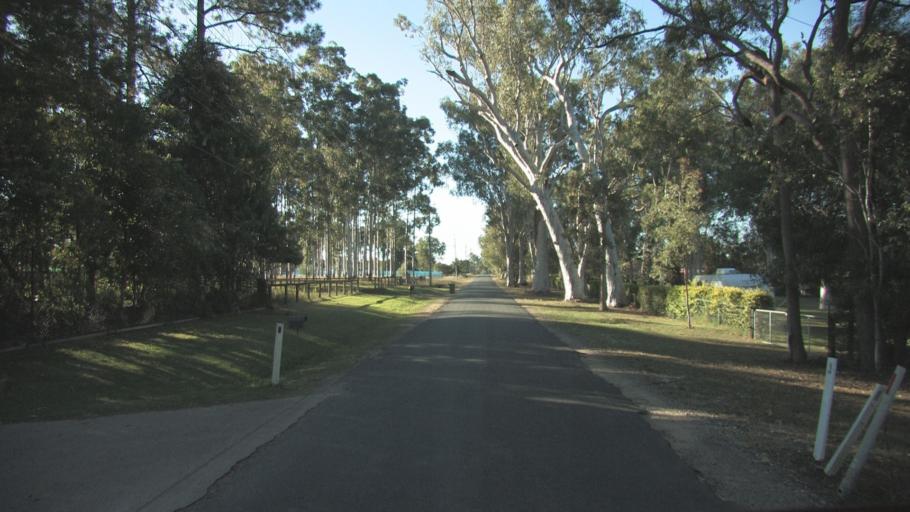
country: AU
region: Queensland
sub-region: Logan
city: Chambers Flat
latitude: -27.7809
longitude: 153.0873
